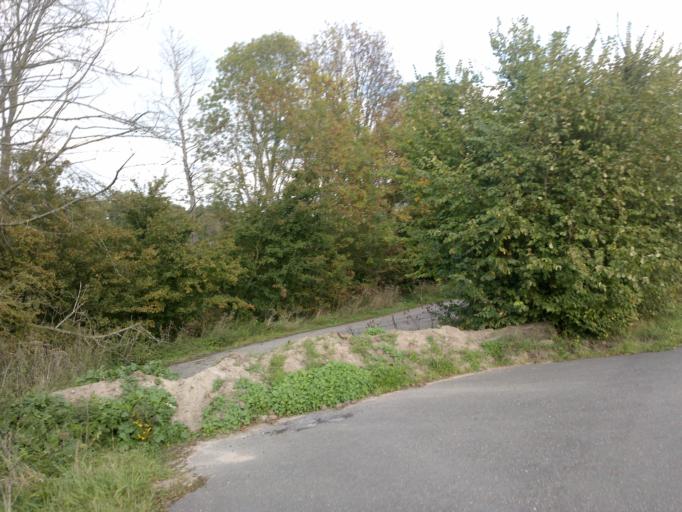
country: NL
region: South Holland
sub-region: Gemeente Sliedrecht
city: Sliedrecht
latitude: 51.7792
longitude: 4.8010
